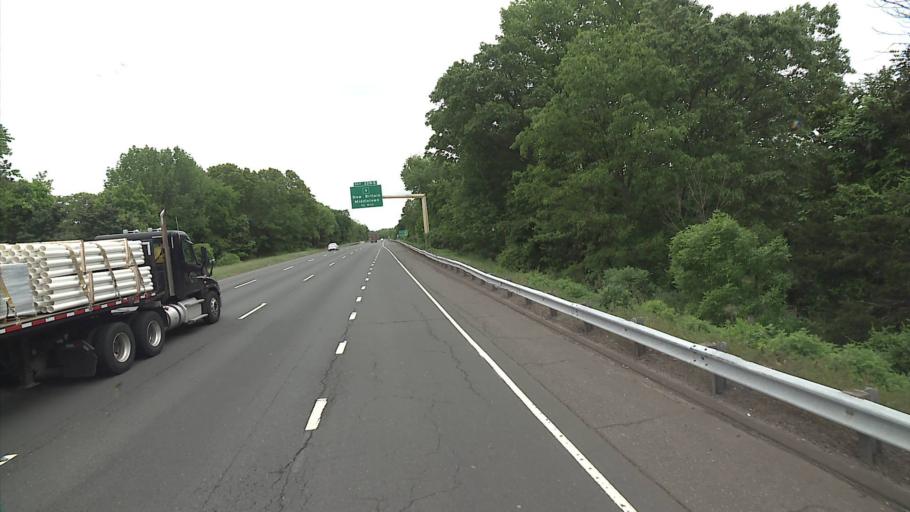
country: US
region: Connecticut
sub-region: Middlesex County
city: Cromwell
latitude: 41.6092
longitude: -72.7005
